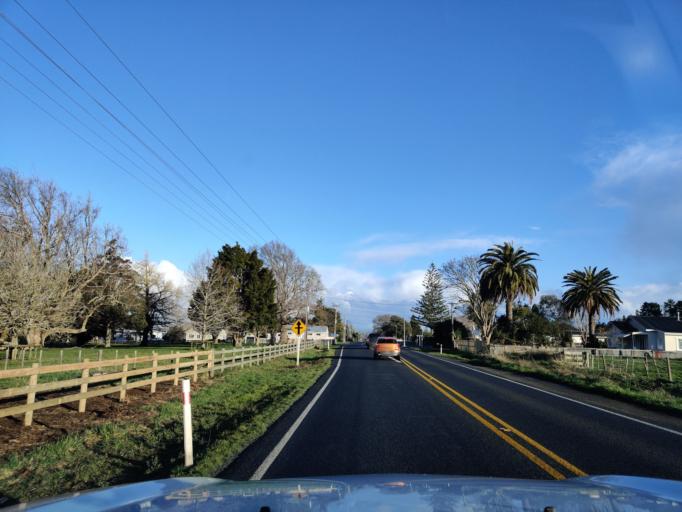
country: NZ
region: Waikato
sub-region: Hauraki District
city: Paeroa
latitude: -37.5881
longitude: 175.5021
